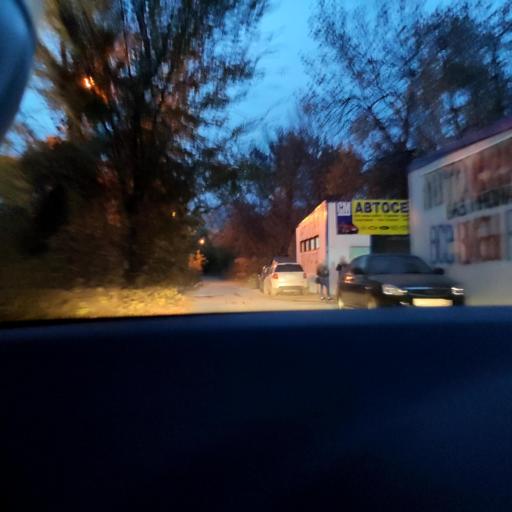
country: RU
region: Samara
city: Samara
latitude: 53.2359
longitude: 50.2398
